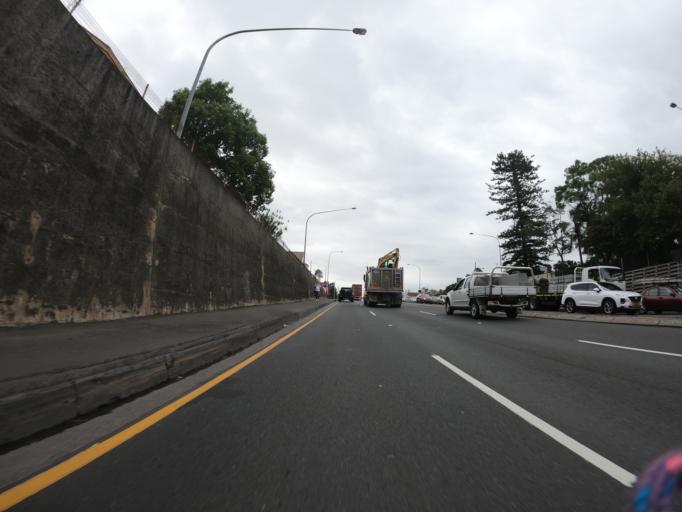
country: AU
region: New South Wales
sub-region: Parramatta
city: Harris Park
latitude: -33.8297
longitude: 151.0042
